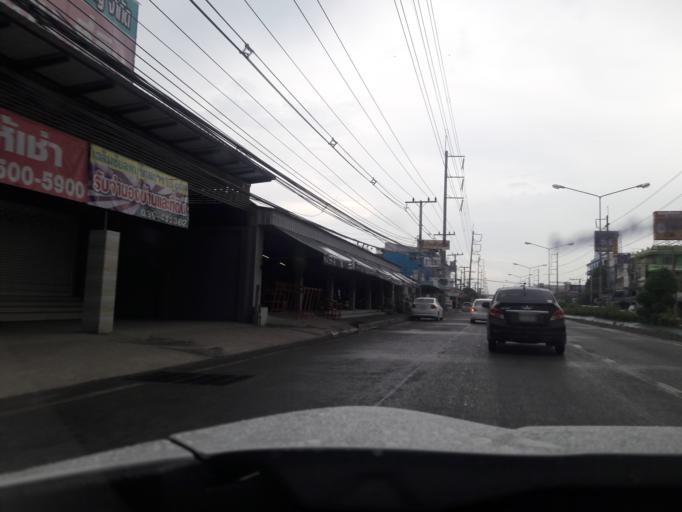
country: TH
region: Lop Buri
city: Lop Buri
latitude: 14.7911
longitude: 100.6730
